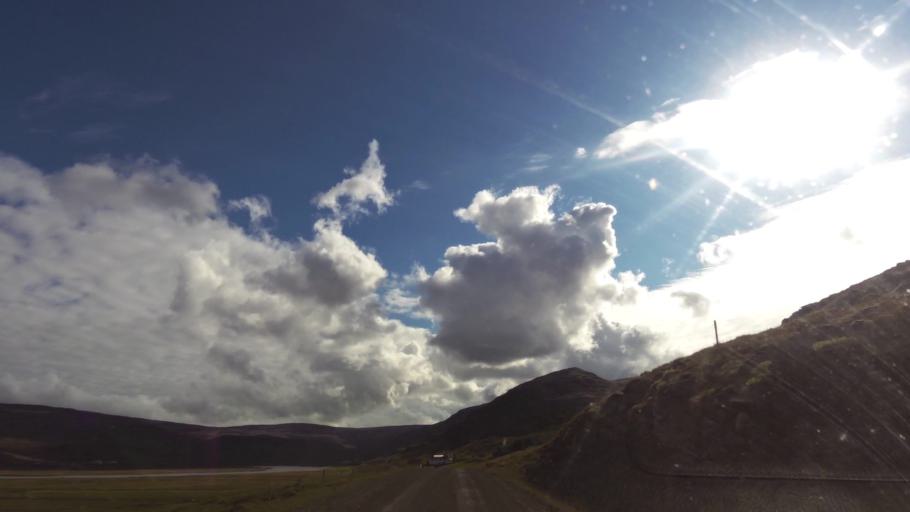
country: IS
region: West
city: Olafsvik
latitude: 65.5794
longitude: -24.1463
